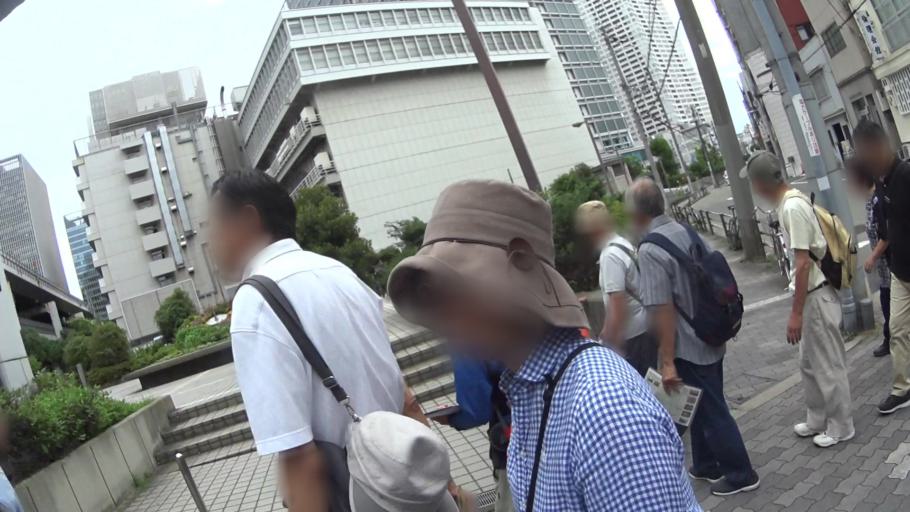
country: JP
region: Osaka
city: Osaka-shi
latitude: 34.6967
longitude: 135.4916
